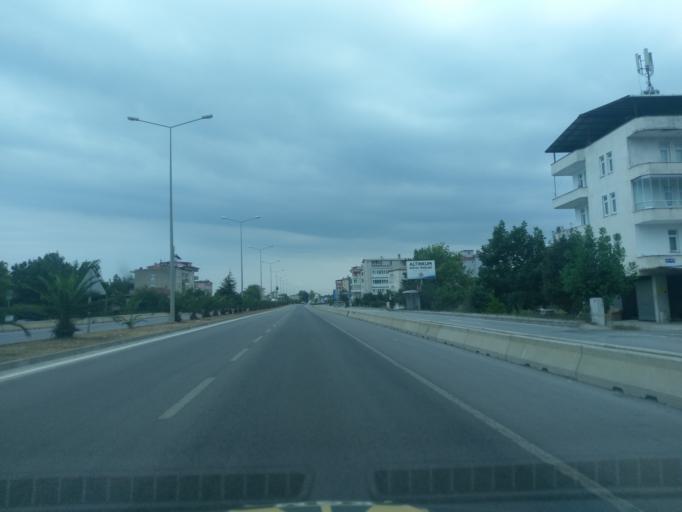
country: TR
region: Samsun
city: Taflan
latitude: 41.4025
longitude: 36.1880
